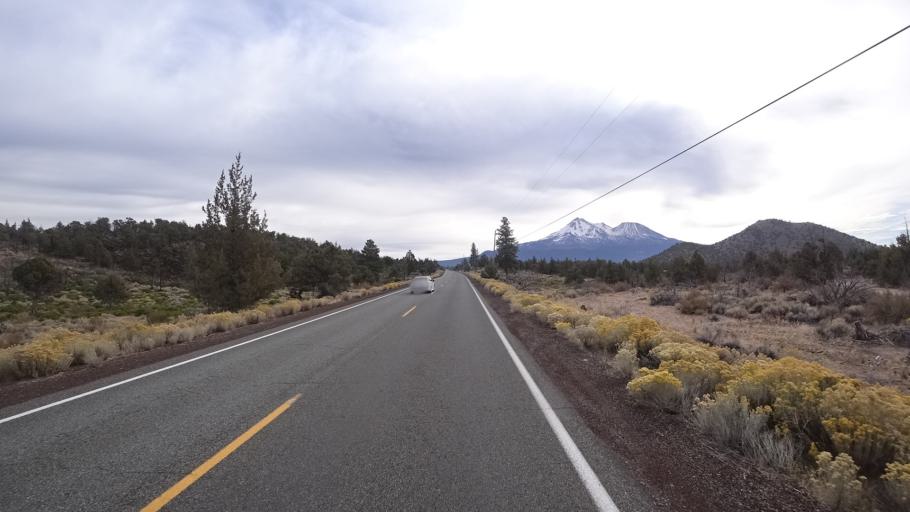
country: US
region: California
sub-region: Siskiyou County
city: Weed
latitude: 41.5608
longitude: -122.2598
